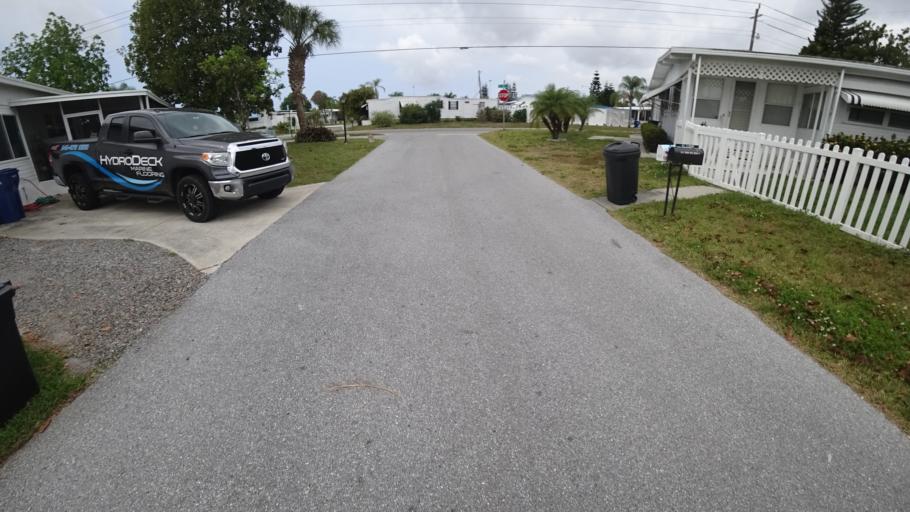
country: US
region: Florida
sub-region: Manatee County
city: South Bradenton
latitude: 27.4501
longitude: -82.5669
